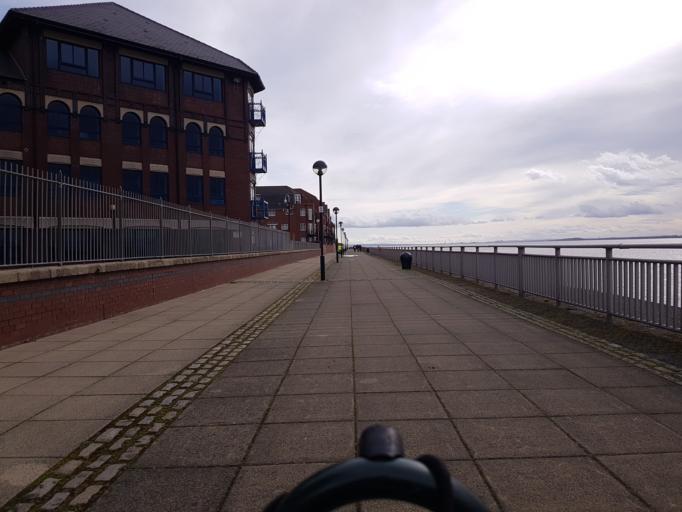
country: GB
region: England
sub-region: Metropolitan Borough of Wirral
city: New Ferry
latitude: 53.3773
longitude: -2.9719
